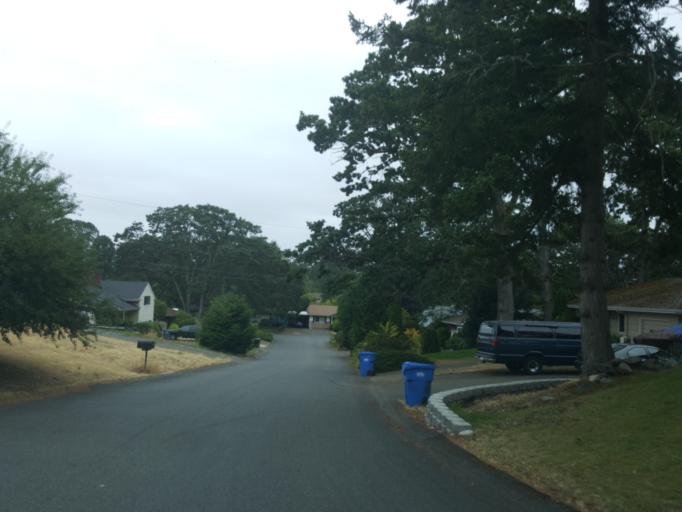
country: US
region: Washington
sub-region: Pierce County
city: McChord Air Force Base
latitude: 47.1636
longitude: -122.4862
